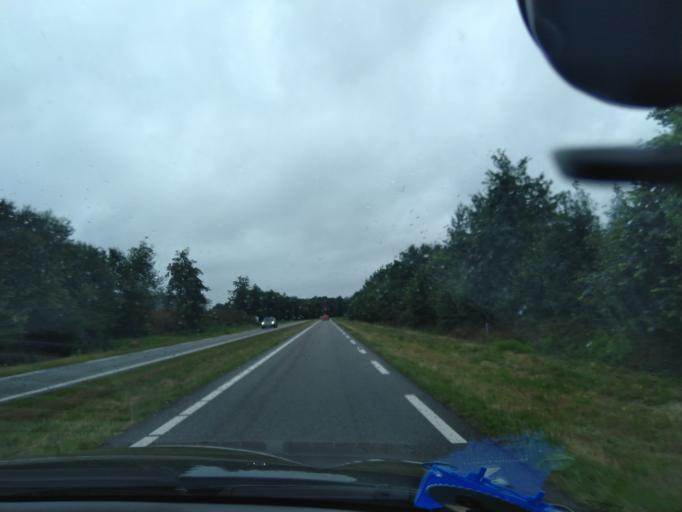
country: DE
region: Lower Saxony
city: Nordhorn
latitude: 52.3833
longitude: 7.0214
